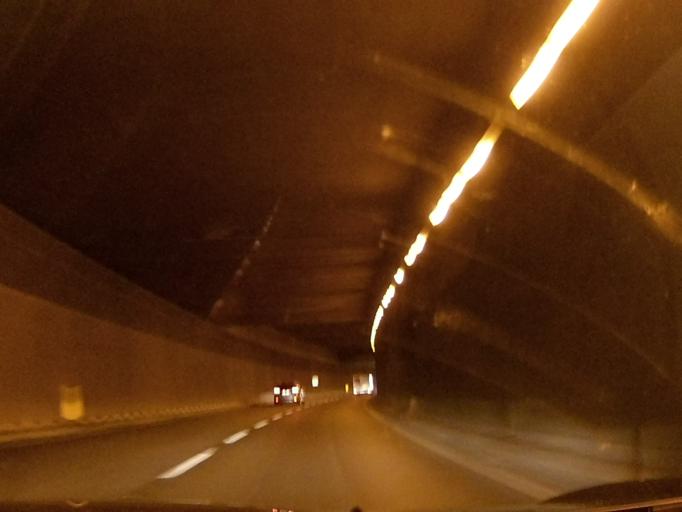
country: IT
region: Lombardy
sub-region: Provincia di Sondrio
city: Piantedo
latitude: 46.1344
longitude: 9.4048
